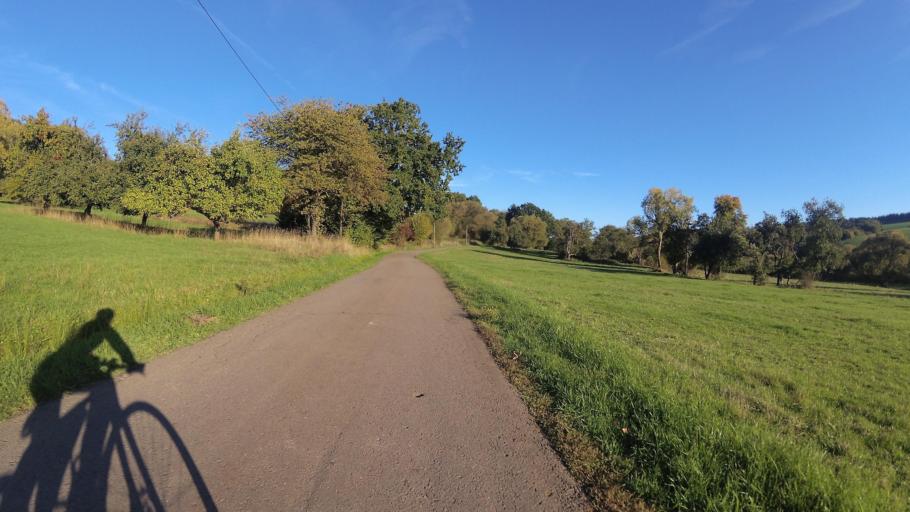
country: DE
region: Saarland
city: Freisen
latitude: 49.5130
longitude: 7.2173
